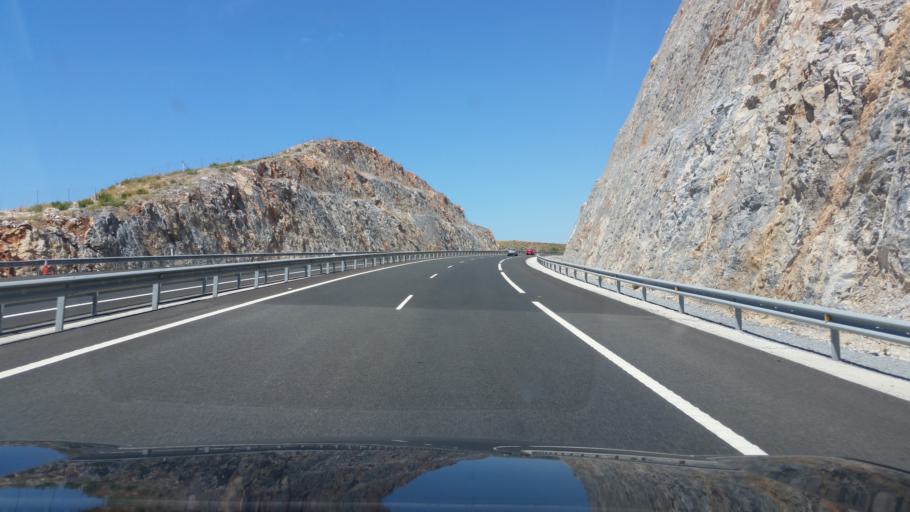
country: ES
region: Andalusia
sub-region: Provincia de Granada
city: Gualchos
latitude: 36.7101
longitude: -3.4095
